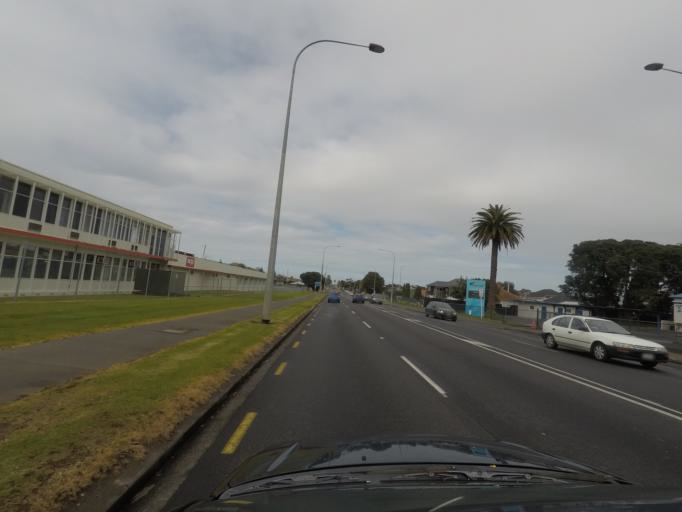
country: NZ
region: Auckland
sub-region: Auckland
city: Tamaki
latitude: -36.9012
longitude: 174.8433
